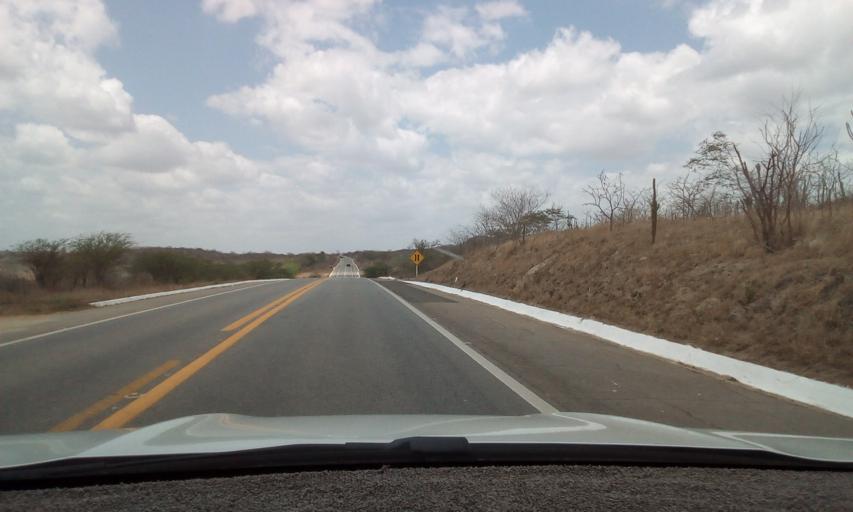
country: BR
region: Pernambuco
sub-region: Taquaritinga Do Norte
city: Taquaritinga do Norte
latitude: -7.7106
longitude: -36.0670
